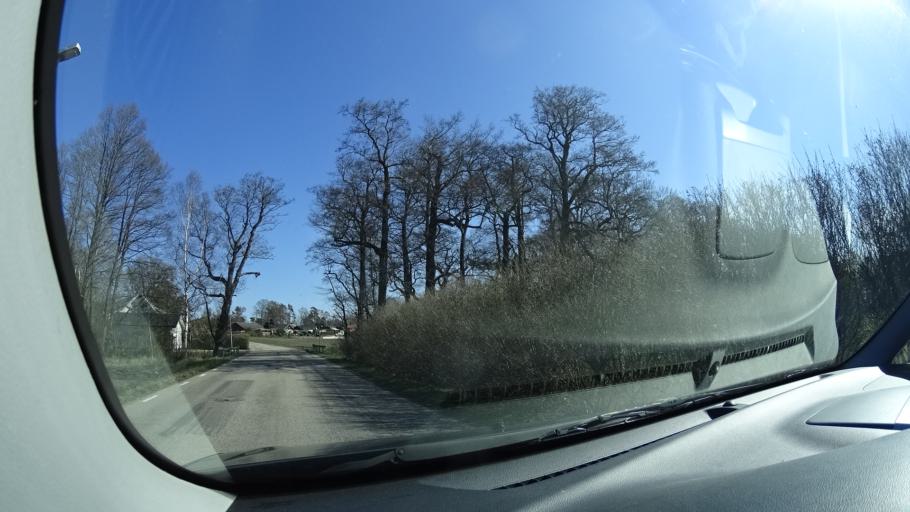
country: SE
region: Skane
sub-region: Hoganas Kommun
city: Hoganas
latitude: 56.2176
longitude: 12.6681
